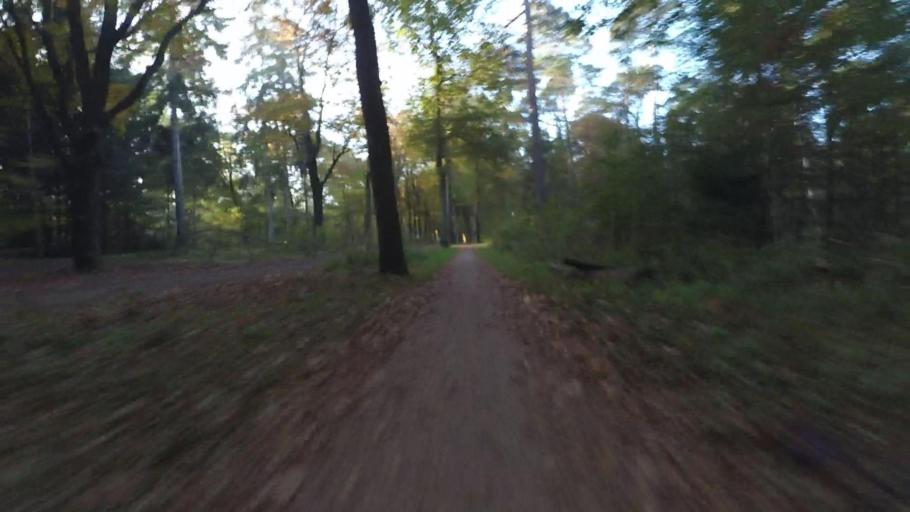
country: NL
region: North Holland
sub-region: Gemeente Hilversum
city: Hilversum
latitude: 52.1700
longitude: 5.2051
